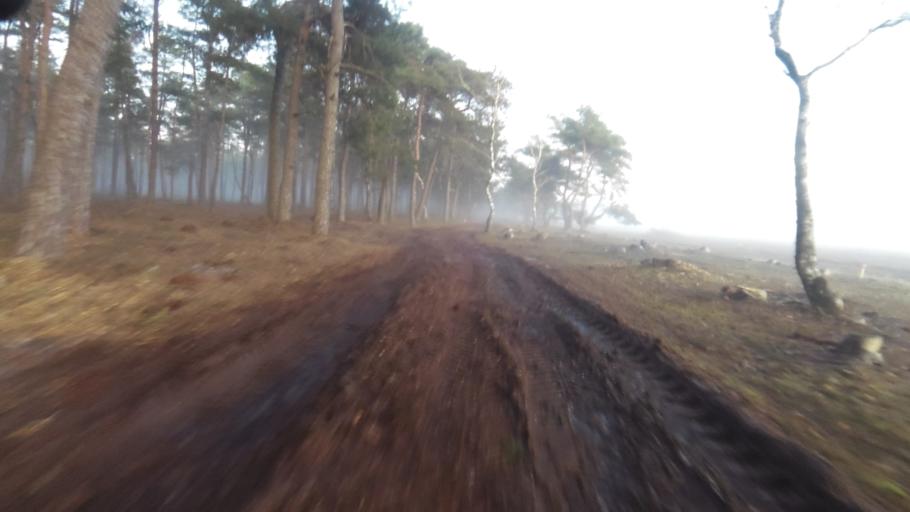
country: NL
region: Gelderland
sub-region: Gemeente Apeldoorn
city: Uddel
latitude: 52.2506
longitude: 5.7973
